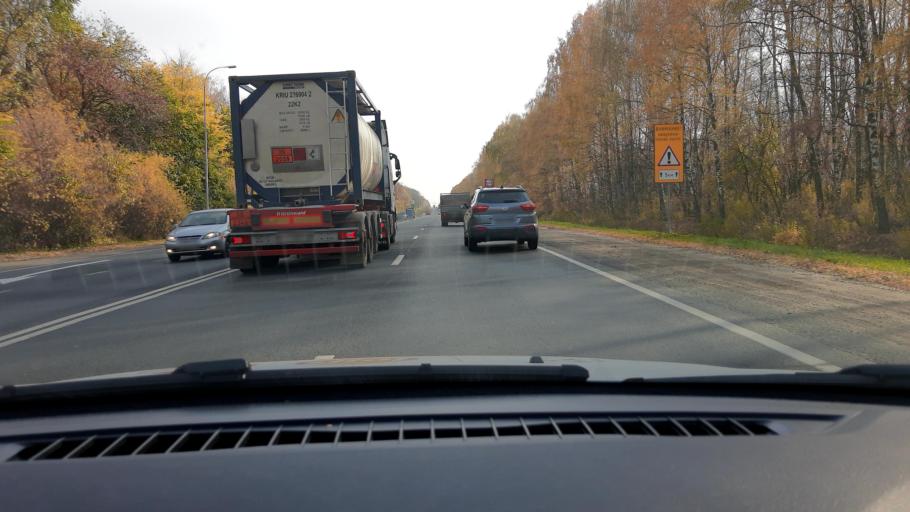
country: RU
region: Nizjnij Novgorod
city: Pamyat' Parizhskoy Kommuny
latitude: 56.0619
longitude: 44.3850
